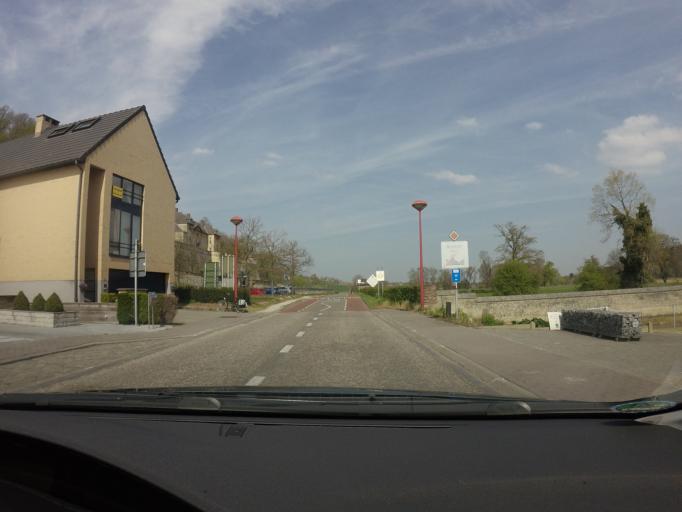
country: NL
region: Limburg
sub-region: Gemeente Maastricht
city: Maastricht
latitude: 50.8176
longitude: 5.6685
